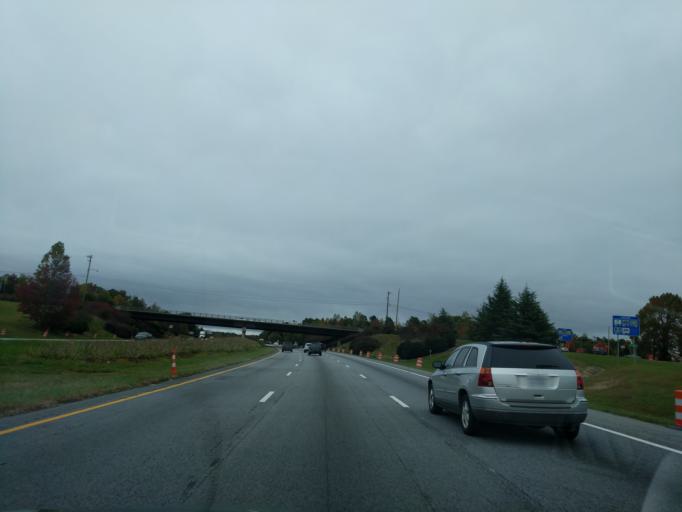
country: US
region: North Carolina
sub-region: Randolph County
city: Archdale
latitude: 35.9021
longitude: -79.9549
